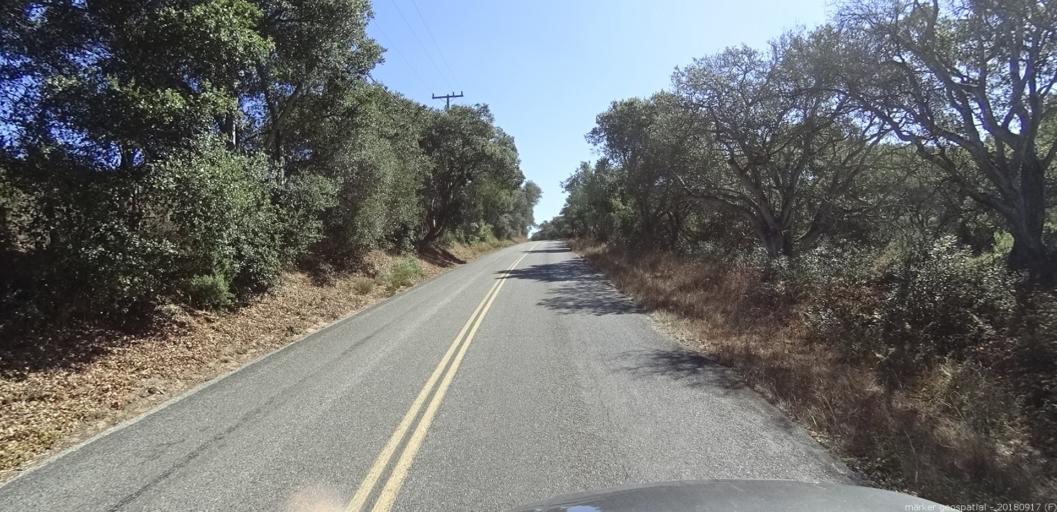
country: US
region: California
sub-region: Monterey County
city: Elkhorn
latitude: 36.8327
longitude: -121.6869
